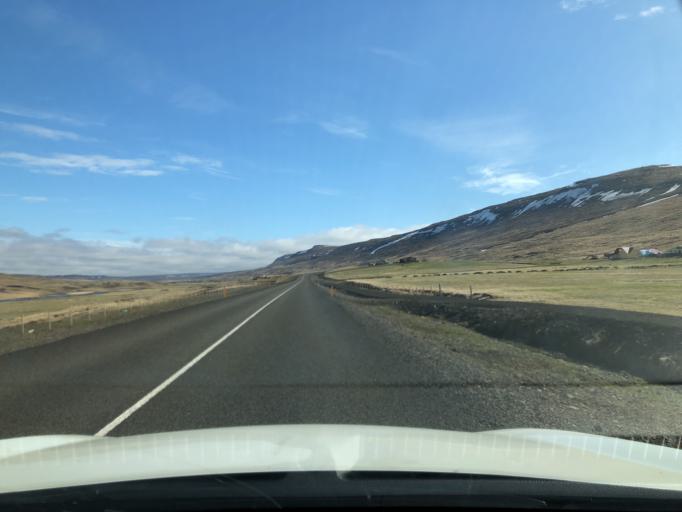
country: IS
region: West
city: Borgarnes
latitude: 65.1479
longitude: -21.5807
